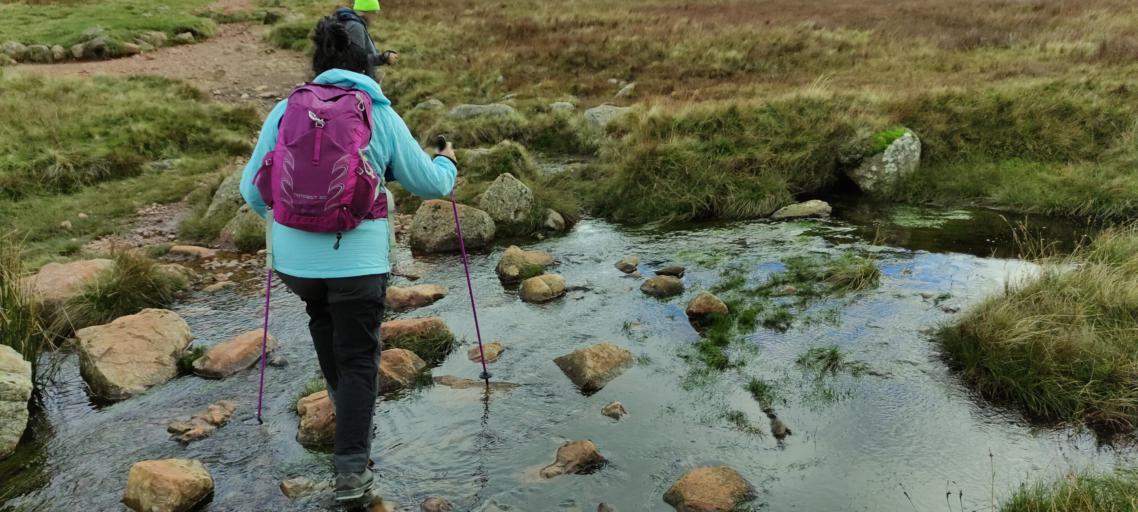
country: GB
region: England
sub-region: Cumbria
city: Ambleside
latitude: 54.4252
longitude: -3.1317
